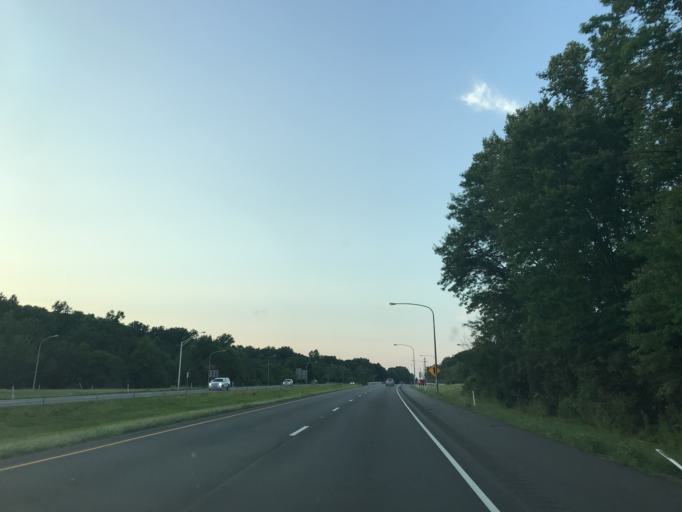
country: US
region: Pennsylvania
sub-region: Bucks County
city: Langhorne Manor
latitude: 40.1668
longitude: -74.8997
